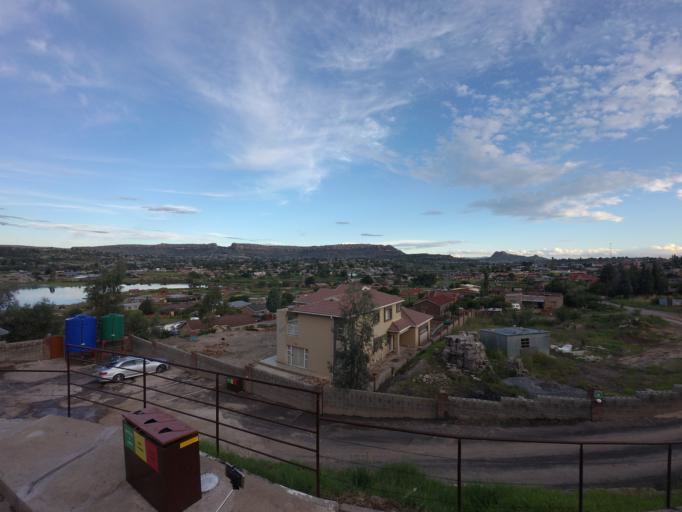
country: LS
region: Maseru
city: Maseru
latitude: -29.3050
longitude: 27.5072
